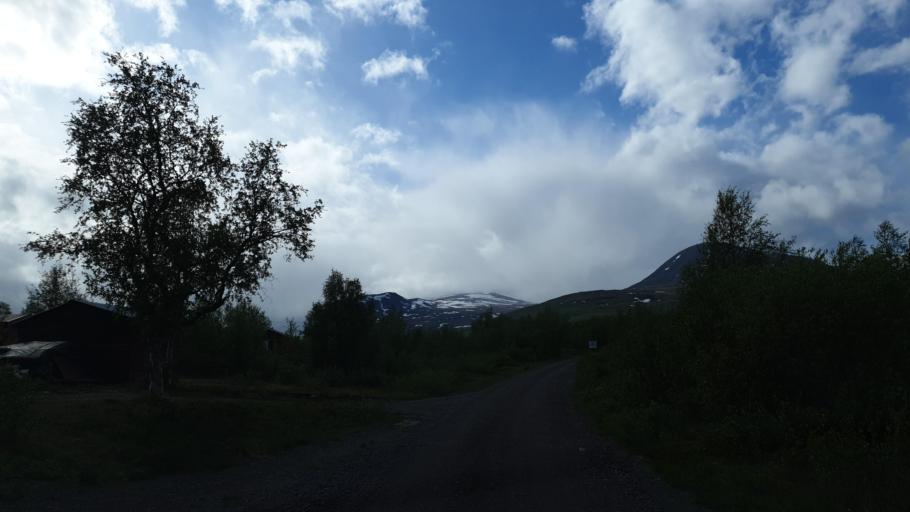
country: SE
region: Norrbotten
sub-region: Kiruna Kommun
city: Kiruna
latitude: 67.8510
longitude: 19.0152
